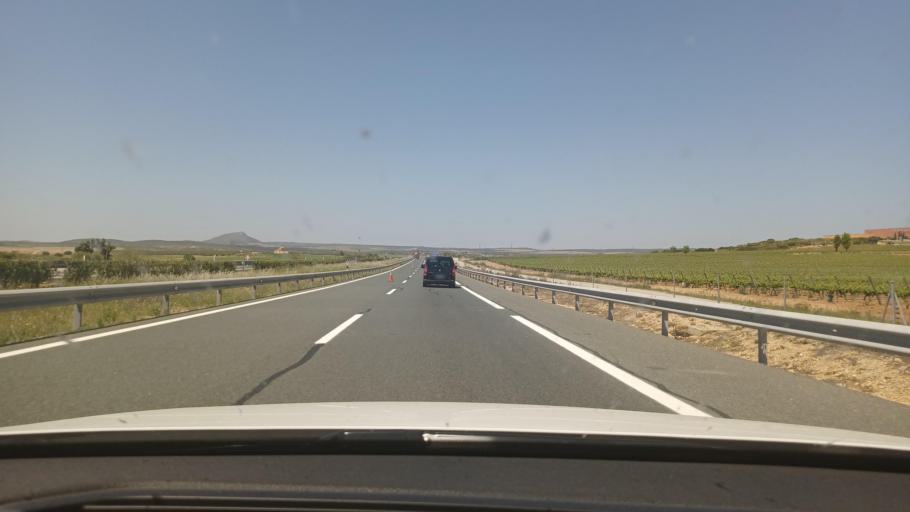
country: ES
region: Castille-La Mancha
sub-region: Provincia de Albacete
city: Alpera
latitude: 38.8796
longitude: -1.2065
